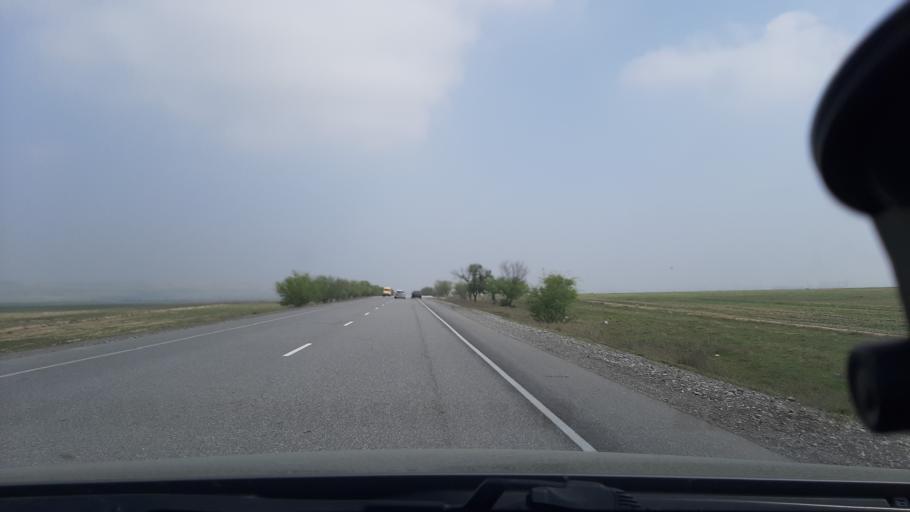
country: UZ
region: Toshkent
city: Bekobod
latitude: 40.1096
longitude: 69.1896
